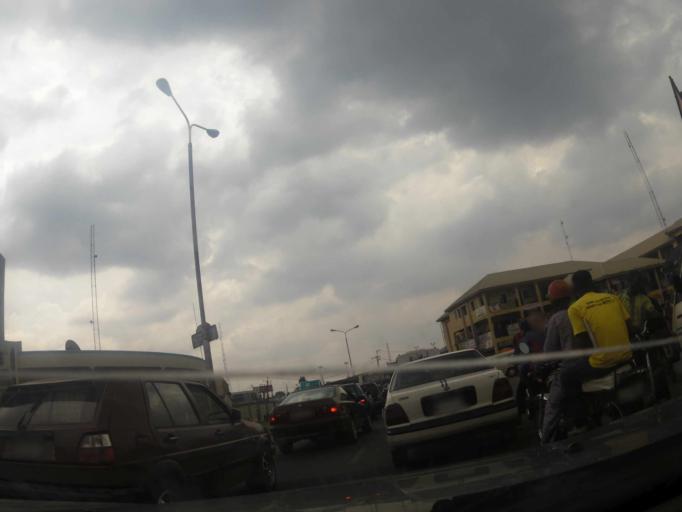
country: NG
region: Oyo
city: Ibadan
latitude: 7.3902
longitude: 3.8791
